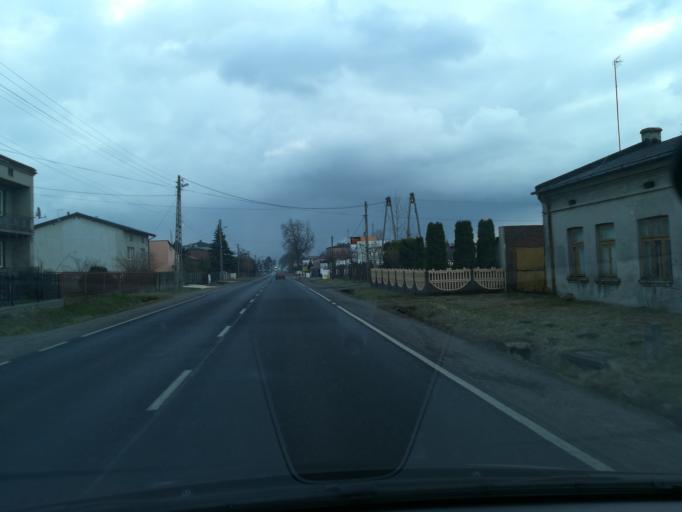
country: PL
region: Lodz Voivodeship
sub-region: Powiat radomszczanski
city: Radomsko
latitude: 51.0764
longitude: 19.4014
